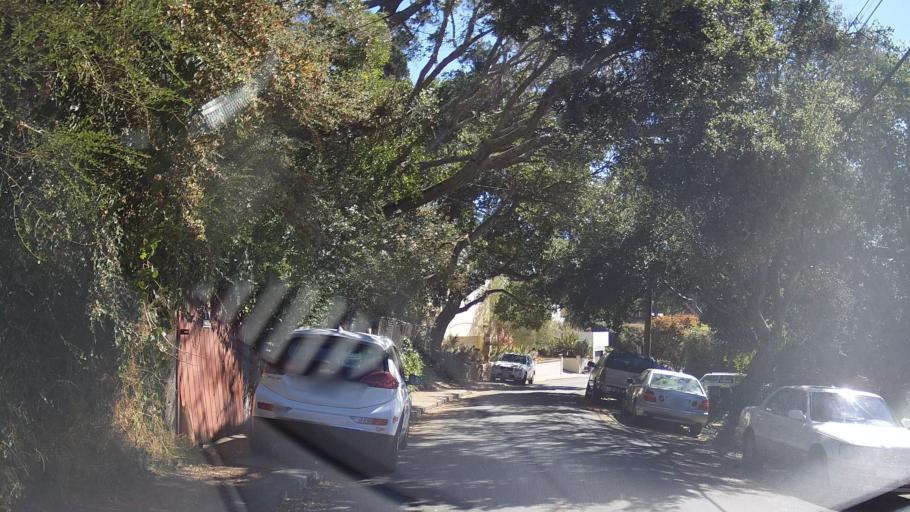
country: US
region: California
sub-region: Alameda County
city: Berkeley
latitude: 37.8927
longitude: -122.2662
